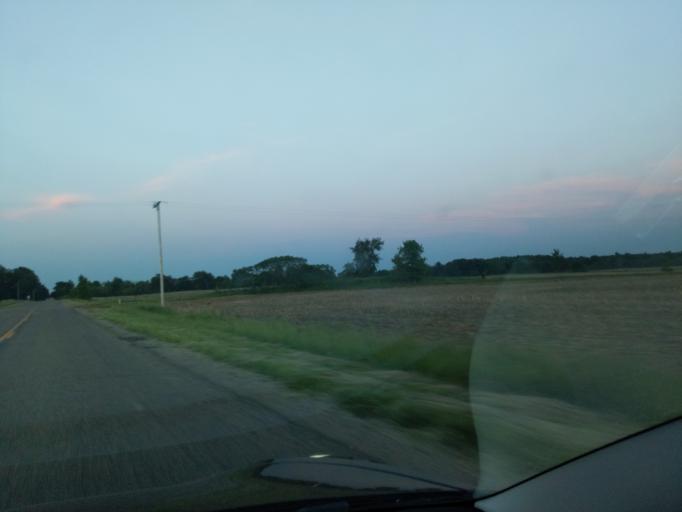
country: US
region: Michigan
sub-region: Eaton County
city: Olivet
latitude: 42.5385
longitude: -84.9554
